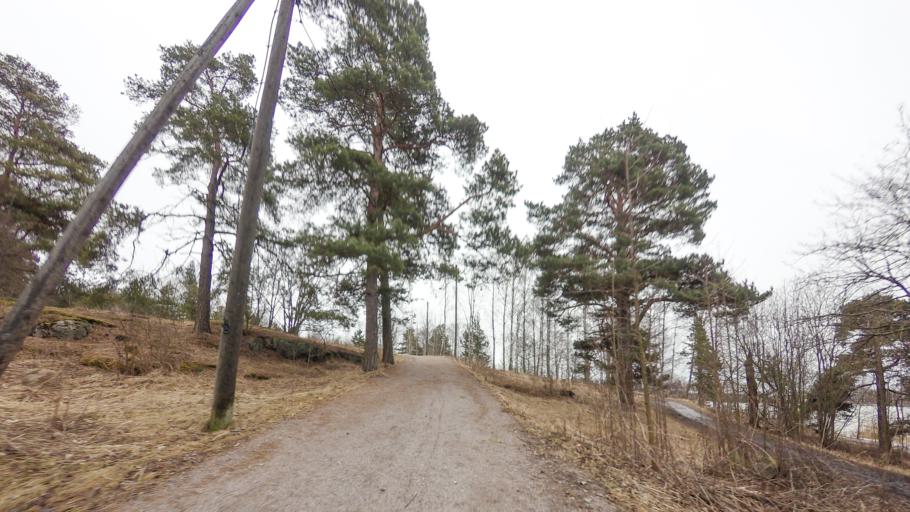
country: FI
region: Uusimaa
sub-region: Helsinki
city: Helsinki
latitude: 60.1791
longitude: 24.9881
